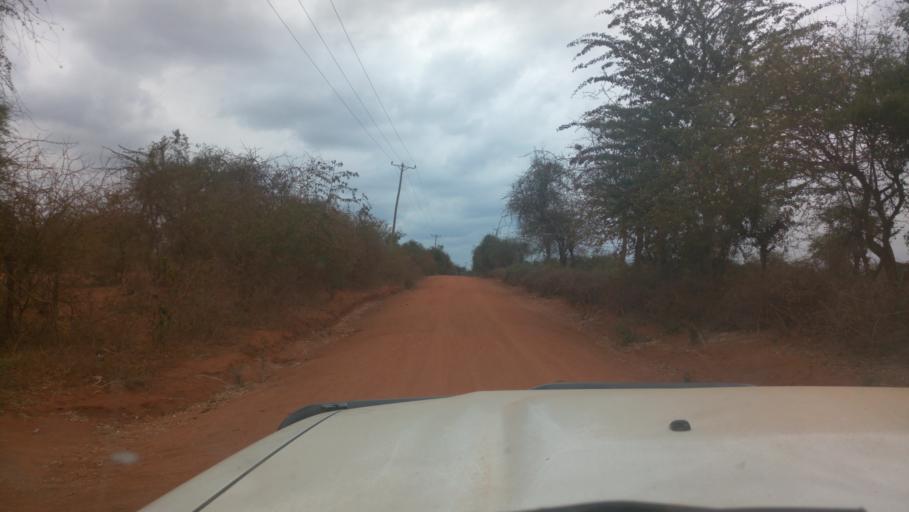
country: KE
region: Makueni
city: Wote
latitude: -1.6524
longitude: 37.8805
